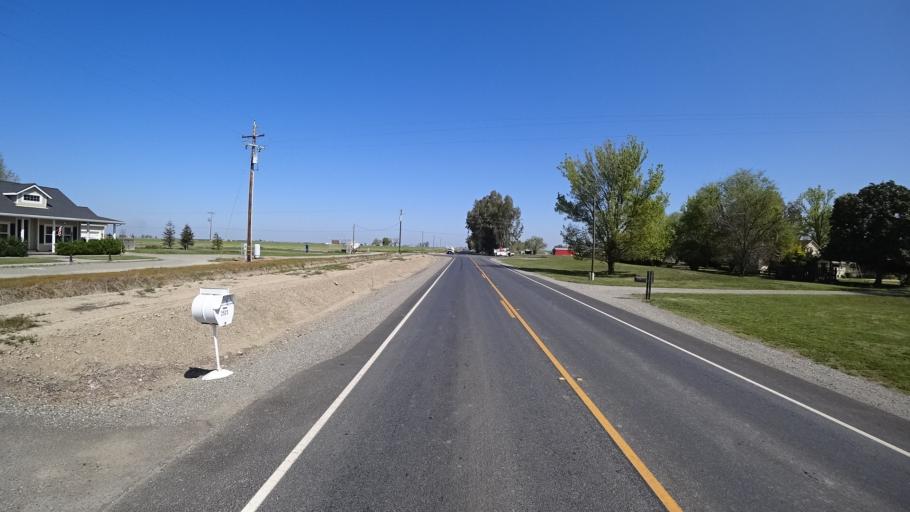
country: US
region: California
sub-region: Glenn County
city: Willows
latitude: 39.5818
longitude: -122.0652
